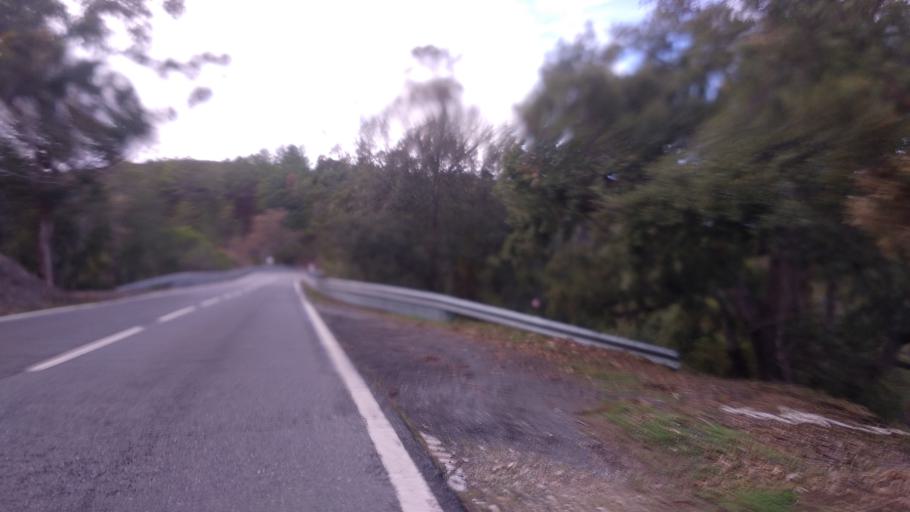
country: PT
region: Faro
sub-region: Sao Bras de Alportel
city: Sao Bras de Alportel
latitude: 37.1805
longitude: -7.9159
